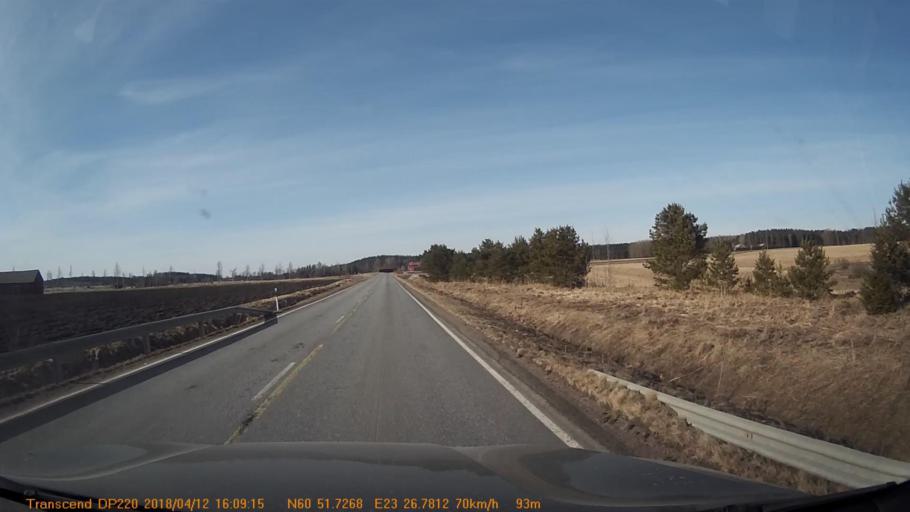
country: FI
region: Haeme
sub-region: Forssa
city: Jokioinen
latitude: 60.8621
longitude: 23.4464
